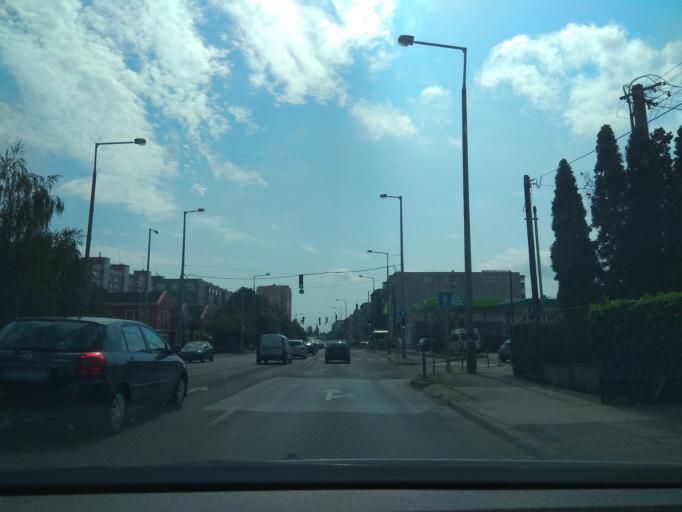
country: HU
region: Heves
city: Eger
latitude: 47.9151
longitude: 20.3698
